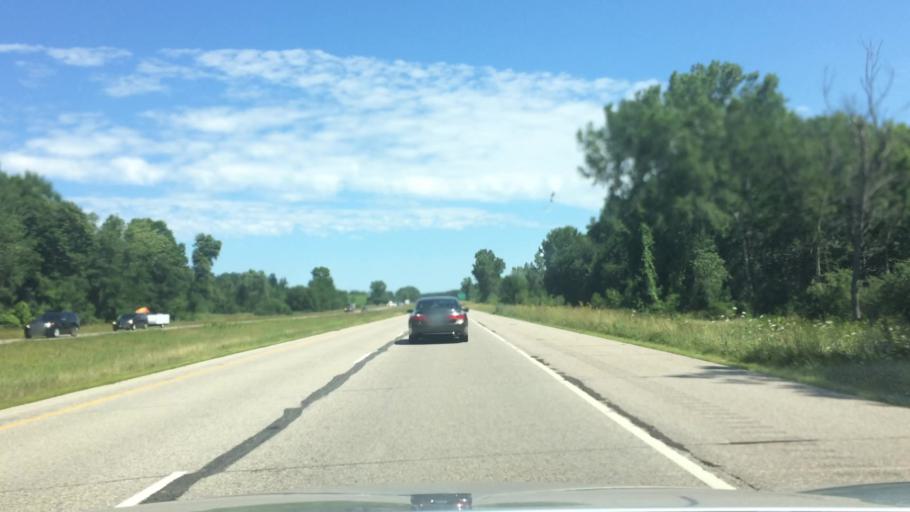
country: US
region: Wisconsin
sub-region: Columbia County
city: Portage
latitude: 43.6766
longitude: -89.4698
